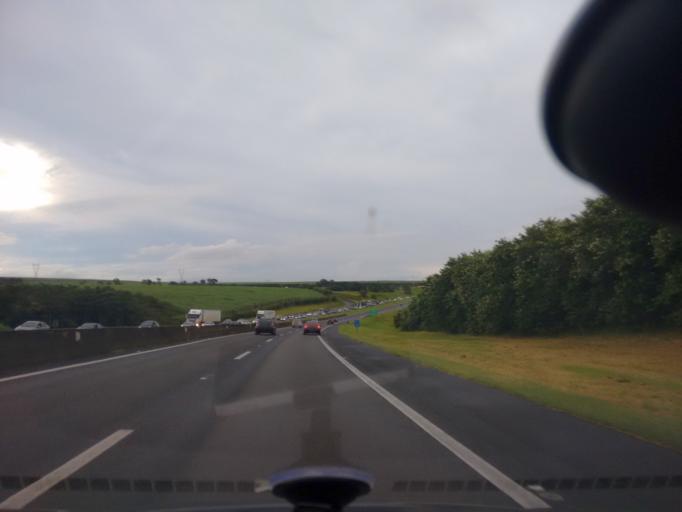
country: BR
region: Sao Paulo
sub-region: Itirapina
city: Itirapina
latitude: -22.2205
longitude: -47.7627
